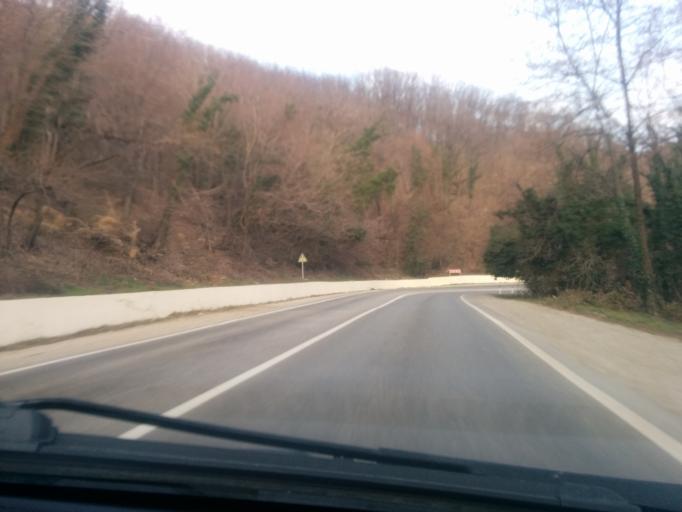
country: RU
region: Krasnodarskiy
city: Nebug
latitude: 44.1741
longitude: 38.9684
